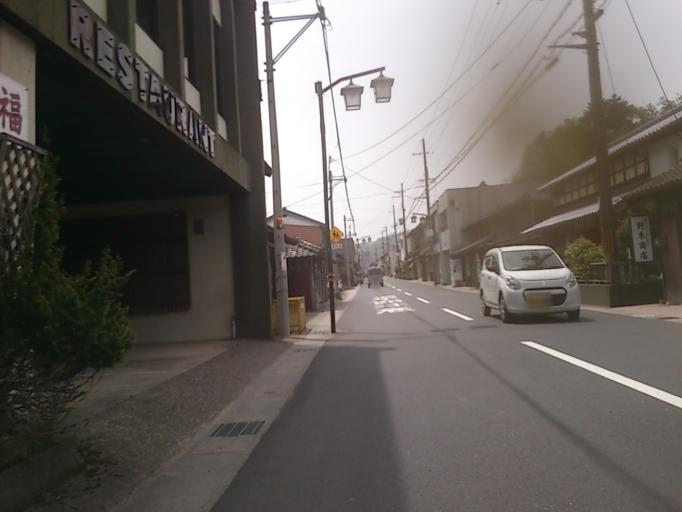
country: JP
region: Kyoto
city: Miyazu
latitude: 35.5810
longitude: 135.0931
